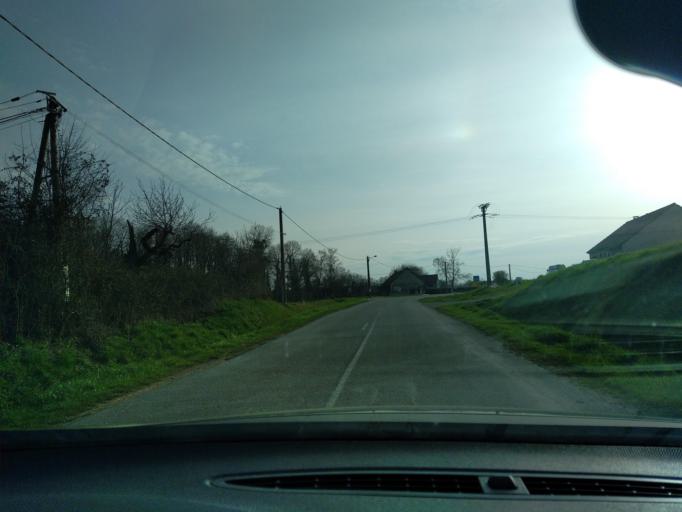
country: FR
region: Franche-Comte
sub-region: Departement du Jura
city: Chaussin
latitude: 46.9836
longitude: 5.4473
